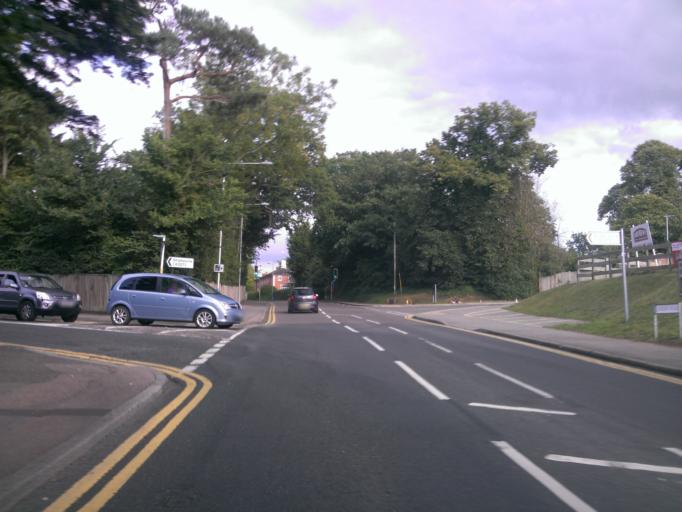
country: GB
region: England
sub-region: Kent
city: Tonbridge
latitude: 51.2034
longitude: 0.2693
